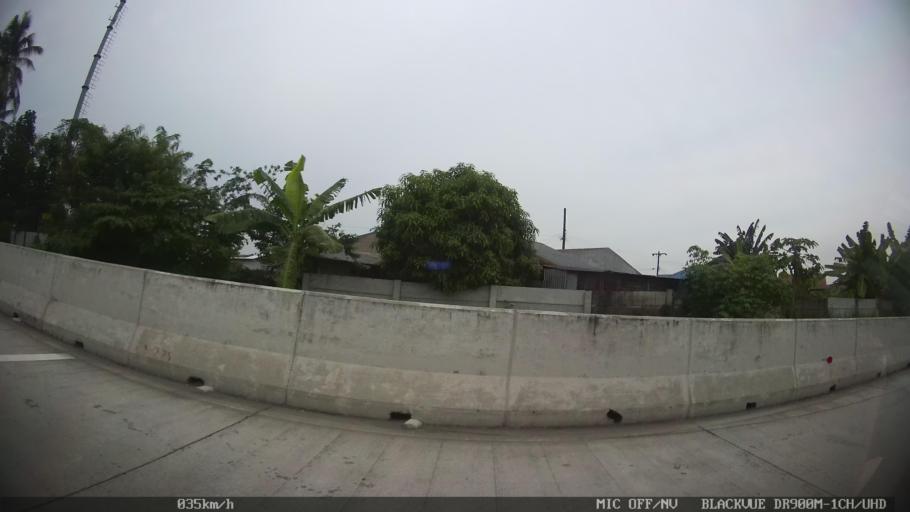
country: ID
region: North Sumatra
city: Deli Tua
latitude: 3.5407
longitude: 98.7240
